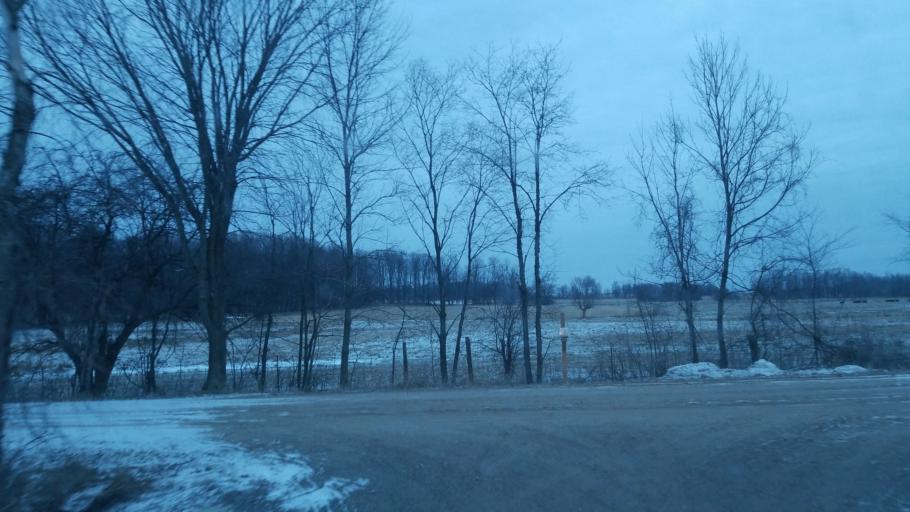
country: US
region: Michigan
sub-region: Osceola County
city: Reed City
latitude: 43.8434
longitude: -85.4079
